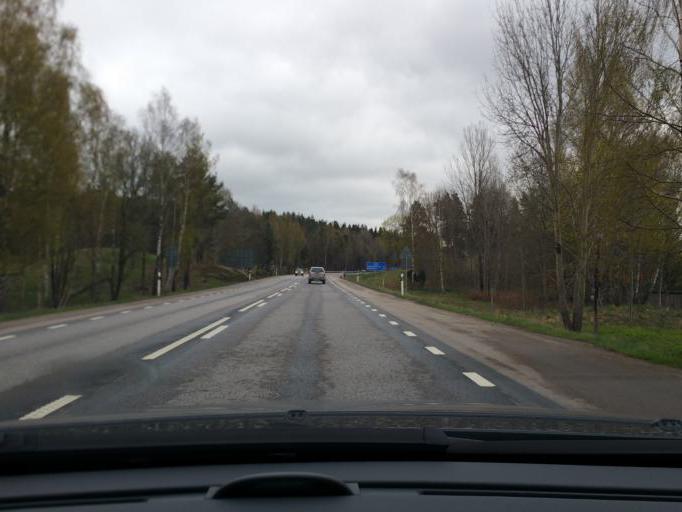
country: SE
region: Kronoberg
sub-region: Vaxjo Kommun
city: Vaexjoe
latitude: 56.8781
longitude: 14.8344
